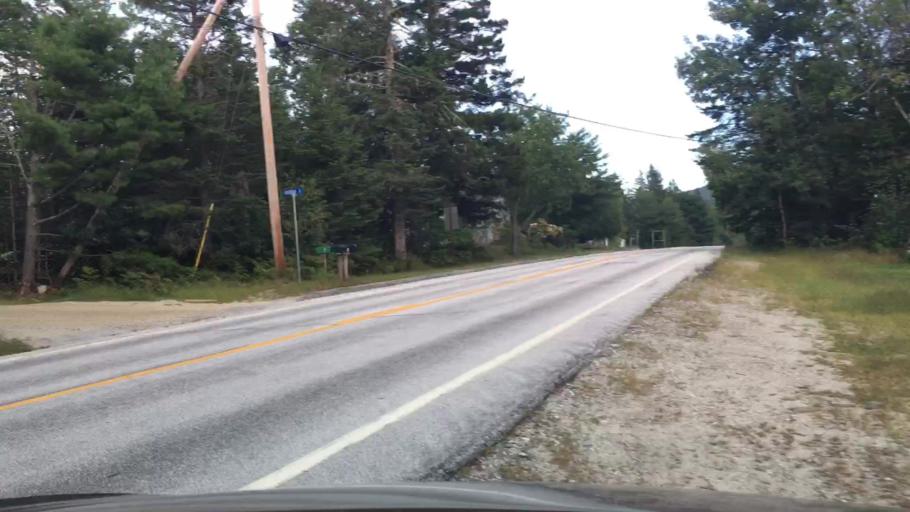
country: US
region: Maine
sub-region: Hancock County
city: Penobscot
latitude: 44.4482
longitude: -68.6173
